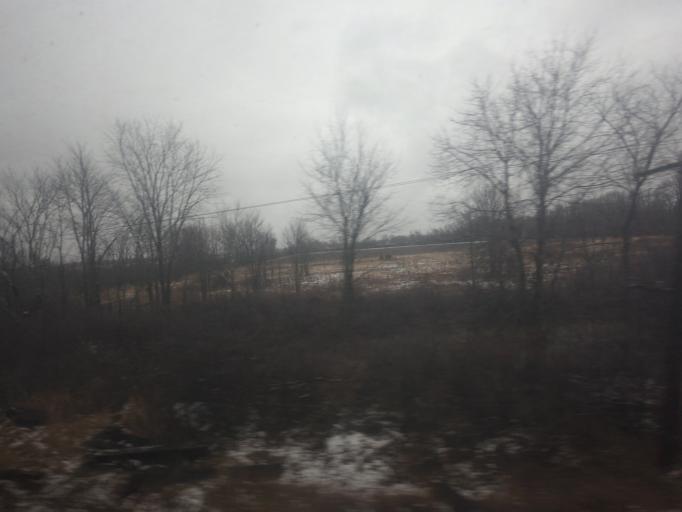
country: CA
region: Ontario
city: Deseronto
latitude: 44.2255
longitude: -77.0655
